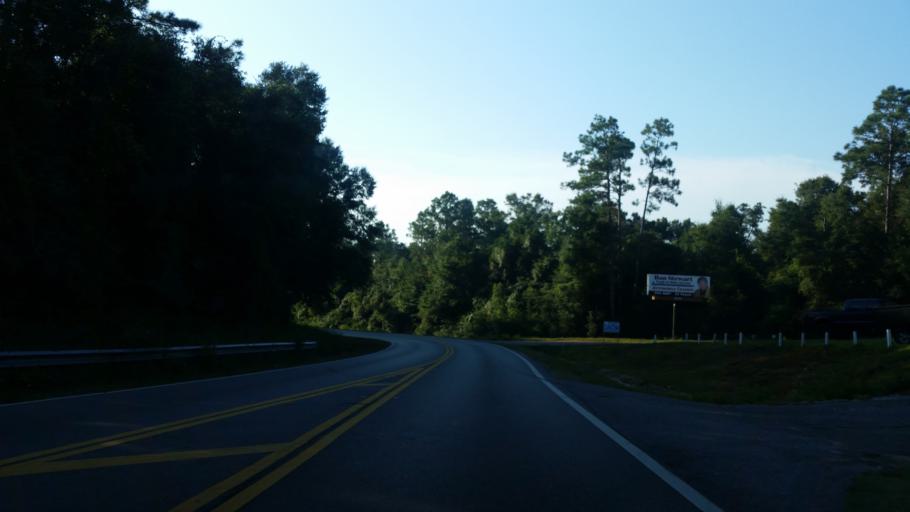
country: US
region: Florida
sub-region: Santa Rosa County
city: Milton
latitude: 30.6163
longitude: -87.0646
